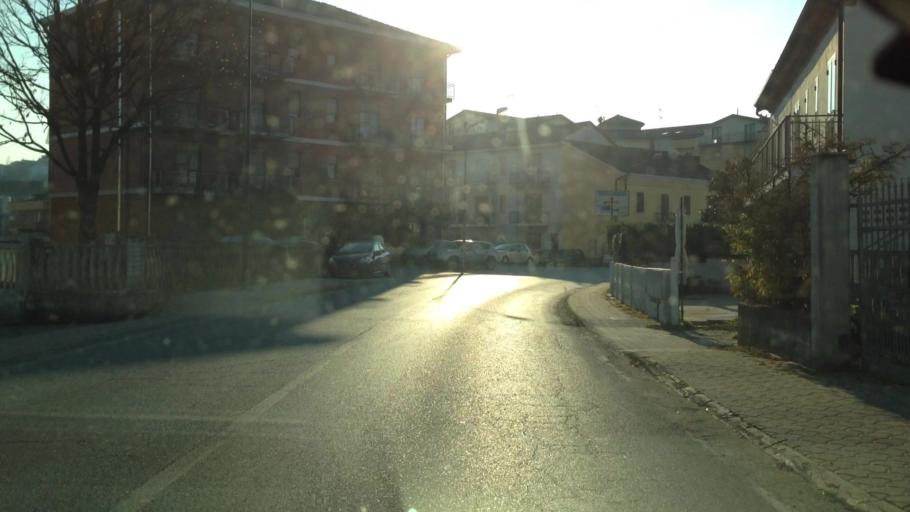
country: IT
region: Piedmont
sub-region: Provincia di Asti
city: Mombercelli
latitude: 44.8237
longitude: 8.2956
